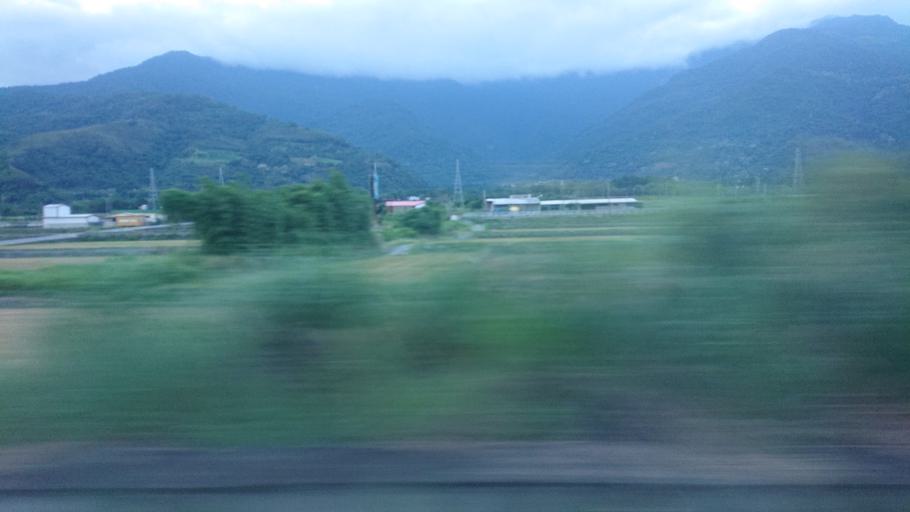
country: TW
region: Taiwan
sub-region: Taitung
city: Taitung
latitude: 23.0352
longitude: 121.1612
